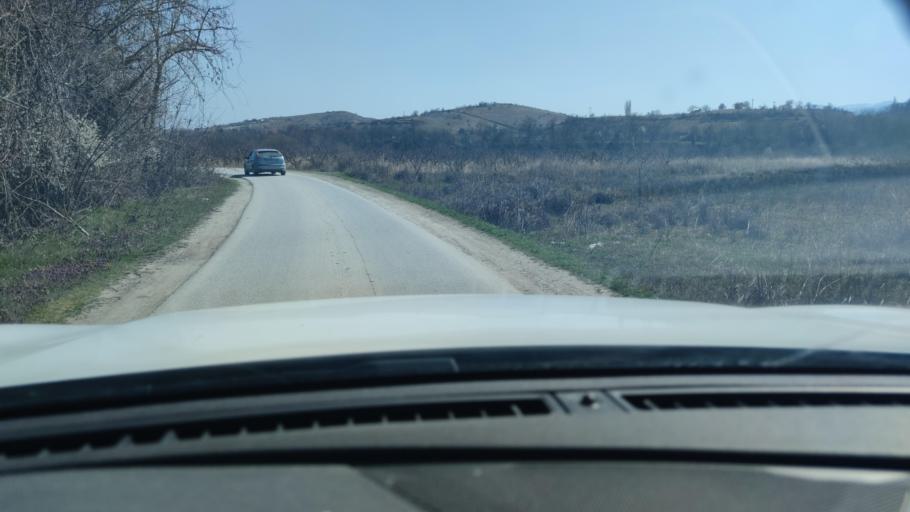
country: MK
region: Rosoman
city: Rosoman
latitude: 41.4738
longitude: 21.9107
